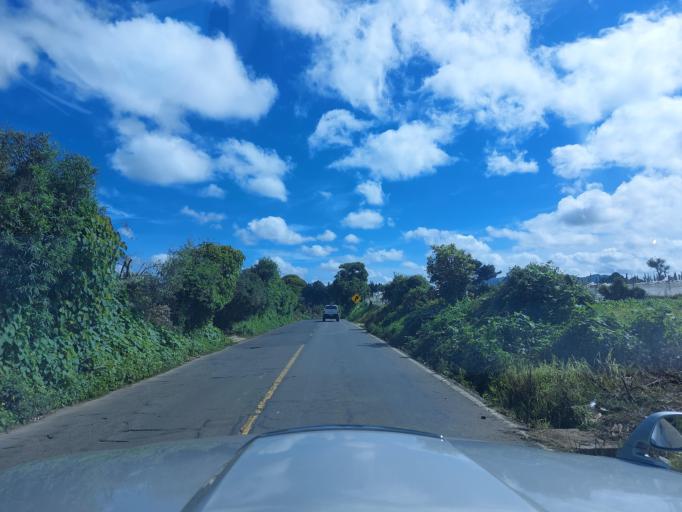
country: GT
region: Chimaltenango
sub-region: Municipio de Zaragoza
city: Zaragoza
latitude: 14.6670
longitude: -90.9007
